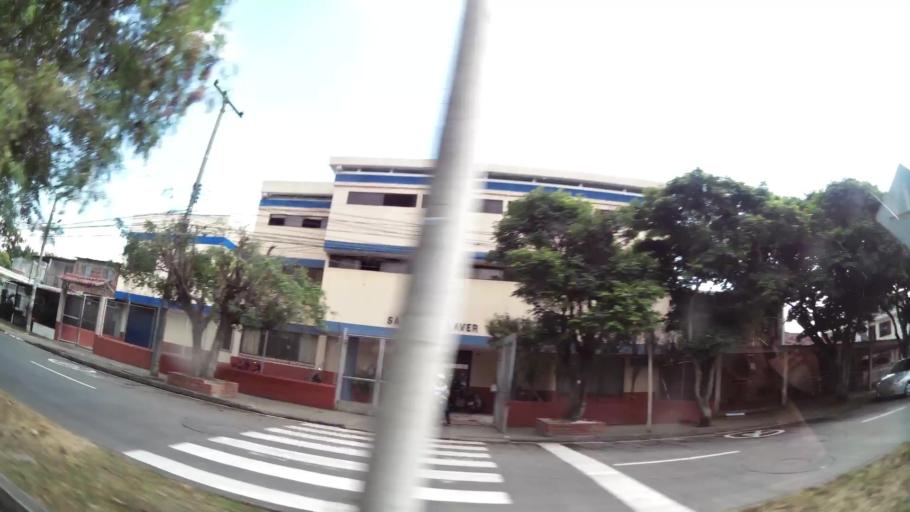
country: CO
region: Valle del Cauca
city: Cali
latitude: 3.4713
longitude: -76.5042
